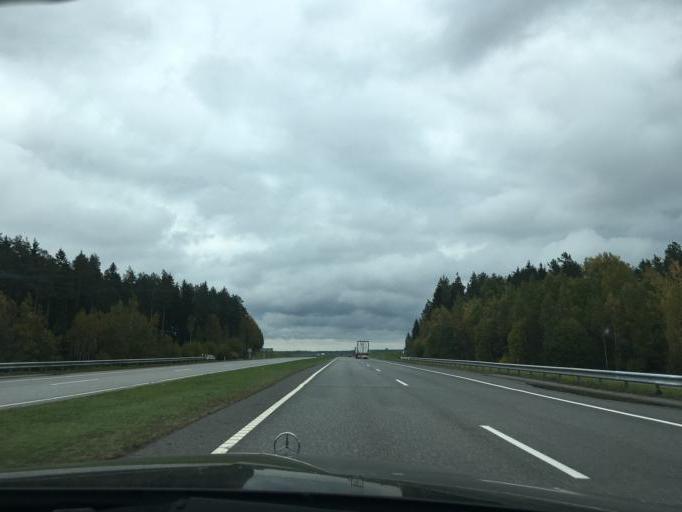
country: BY
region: Vitebsk
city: Kokhanava
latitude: 54.4769
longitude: 29.8523
